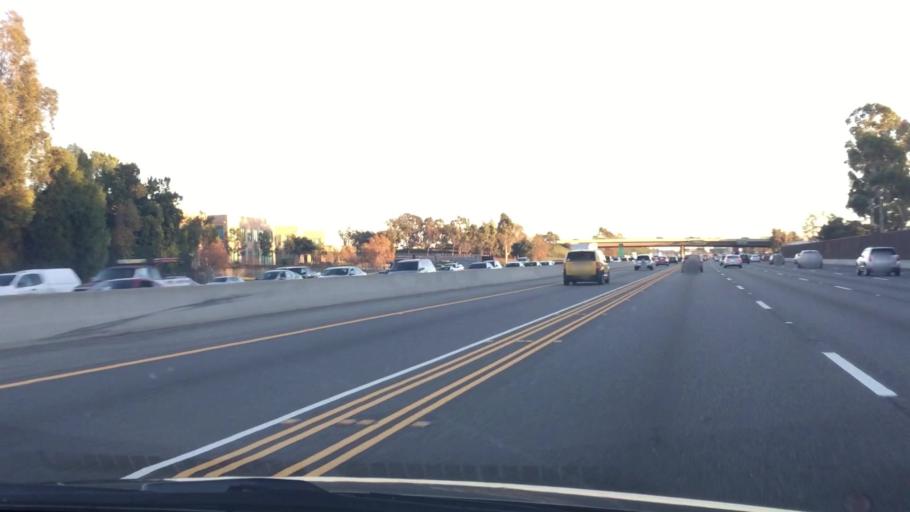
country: US
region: California
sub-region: Orange County
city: Irvine
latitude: 33.6933
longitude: -117.7707
